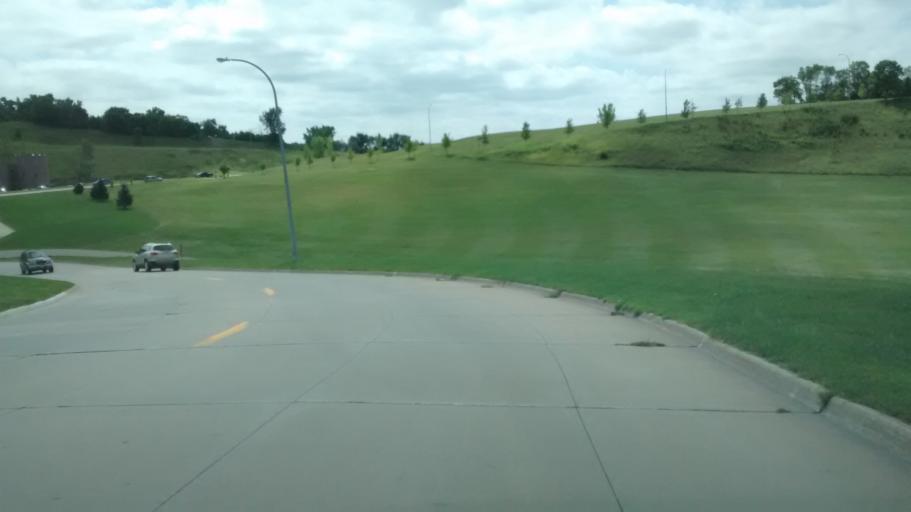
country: US
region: Iowa
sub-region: Woodbury County
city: Sergeant Bluff
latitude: 42.4403
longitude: -96.3508
